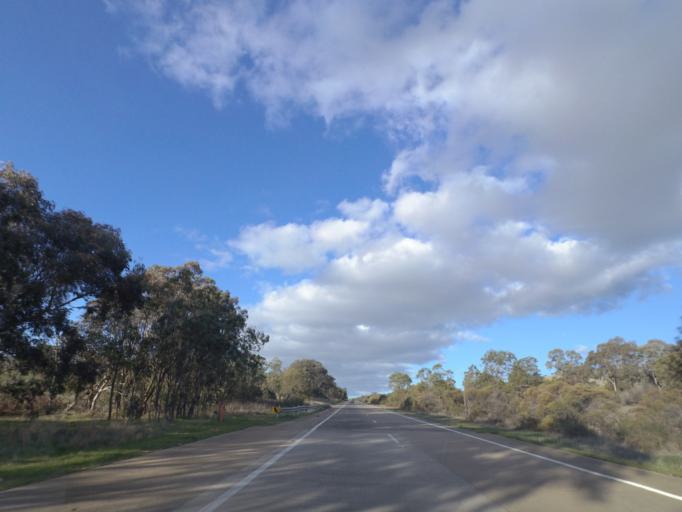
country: AU
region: New South Wales
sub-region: Yass Valley
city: Yass
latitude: -34.8056
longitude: 148.4754
